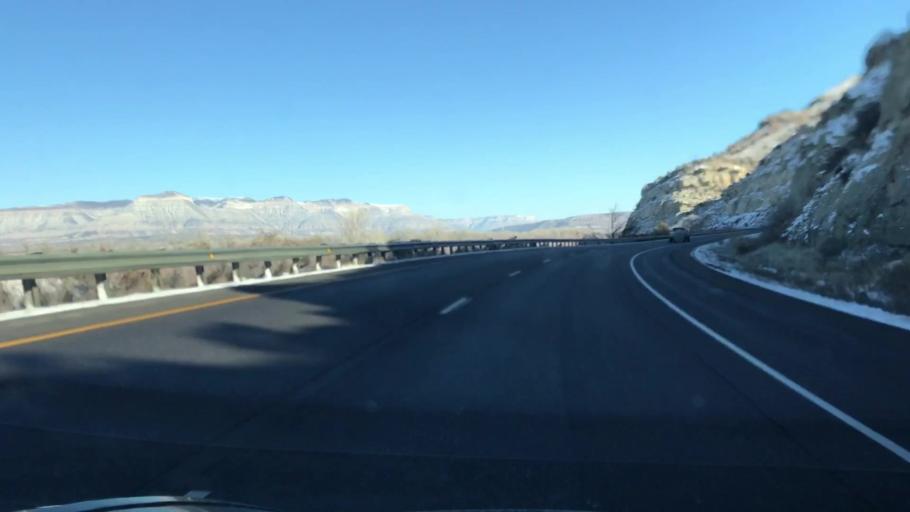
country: US
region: Colorado
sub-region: Mesa County
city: Palisade
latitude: 39.2725
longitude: -108.2474
